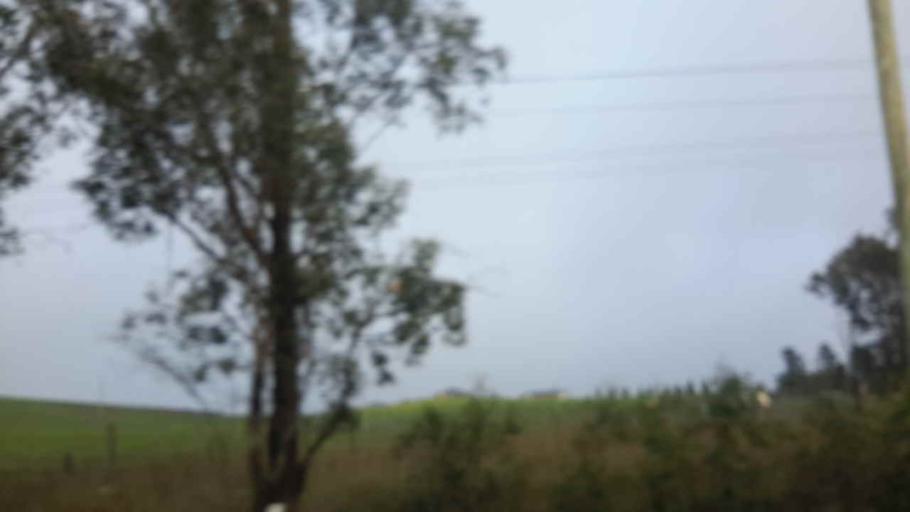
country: AU
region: New South Wales
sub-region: Penrith Municipality
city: Glenmore Park
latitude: -33.8065
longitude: 150.6956
